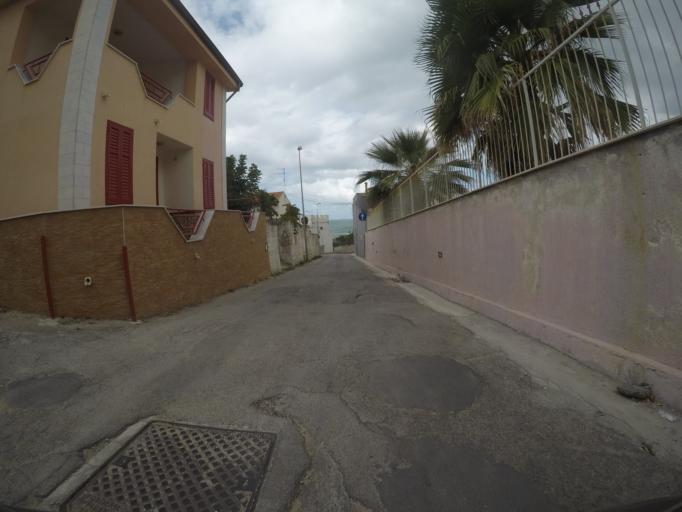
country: IT
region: Sicily
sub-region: Palermo
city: Trappeto
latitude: 38.0722
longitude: 13.0546
